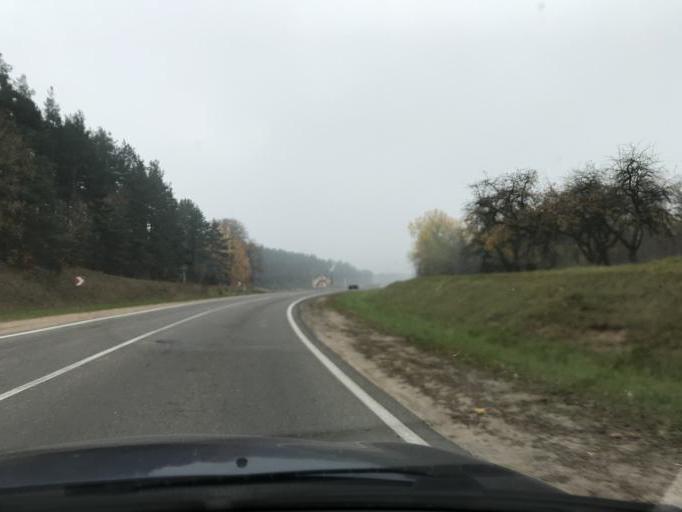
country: BY
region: Grodnenskaya
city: Hrodna
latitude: 53.8105
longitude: 23.8624
